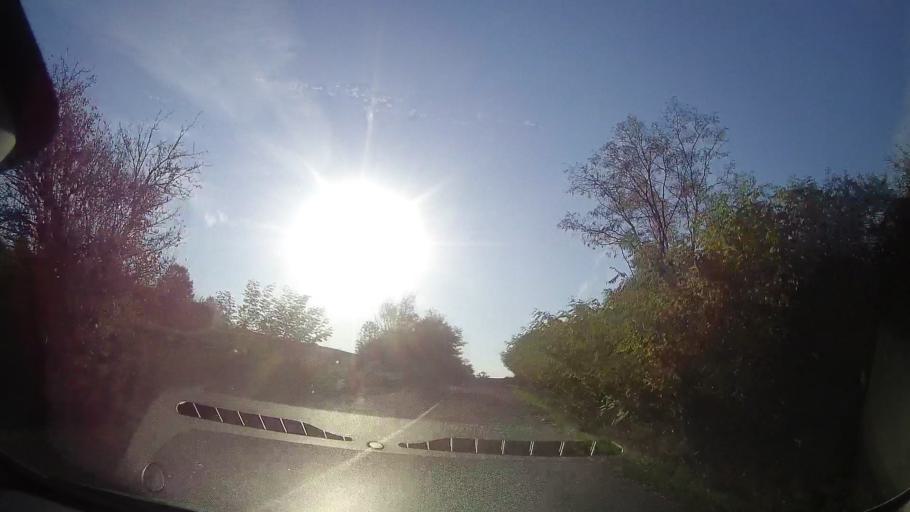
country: RO
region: Timis
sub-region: Comuna Bogda
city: Bogda
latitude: 45.9681
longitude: 21.6071
